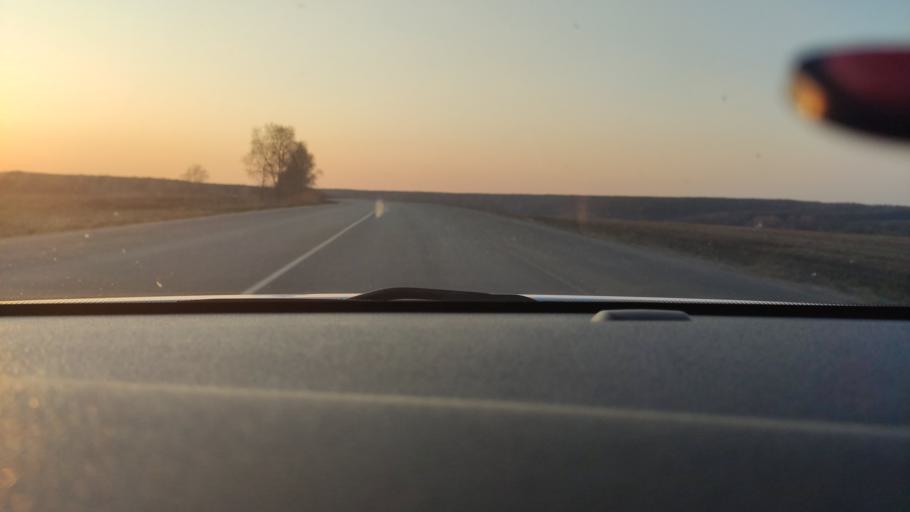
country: RU
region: Voronezj
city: Kolodeznyy
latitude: 51.3357
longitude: 39.0852
